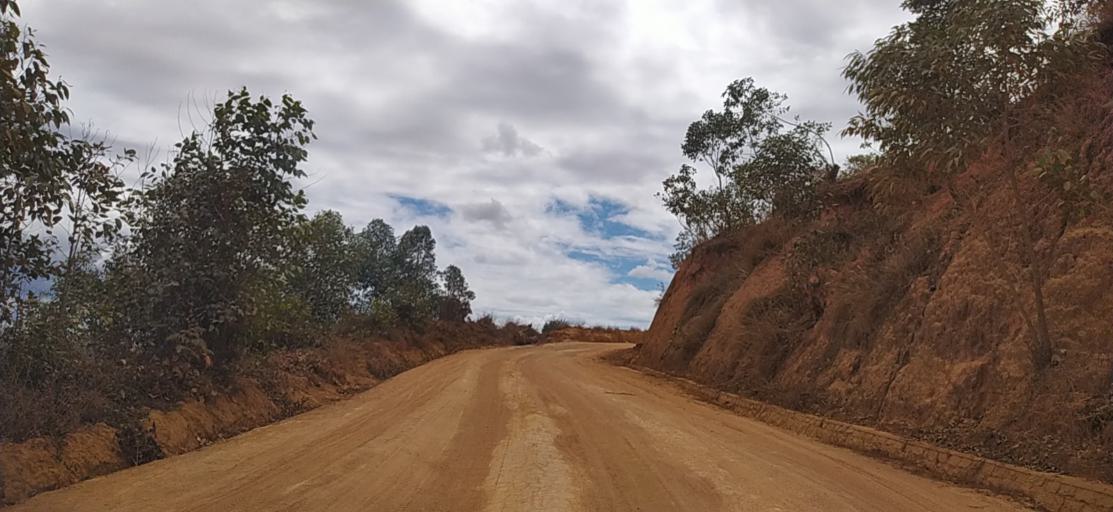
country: MG
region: Alaotra Mangoro
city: Ambatondrazaka
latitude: -17.9979
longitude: 48.2635
